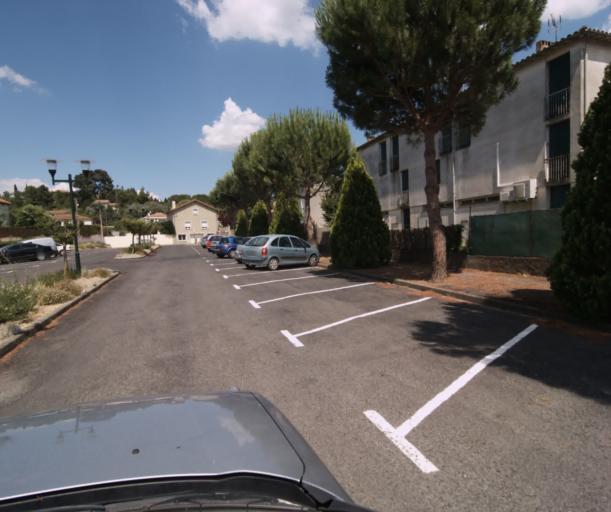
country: FR
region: Languedoc-Roussillon
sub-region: Departement de l'Aude
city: Limoux
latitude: 43.0480
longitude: 2.2238
